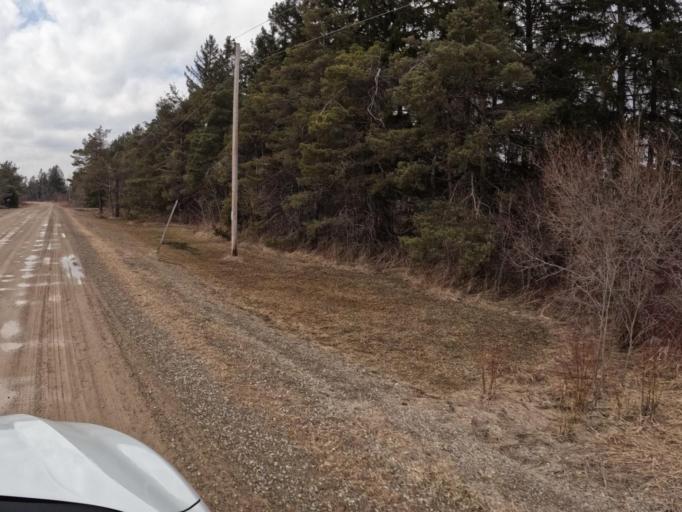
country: CA
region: Ontario
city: Shelburne
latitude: 44.0337
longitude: -80.2328
